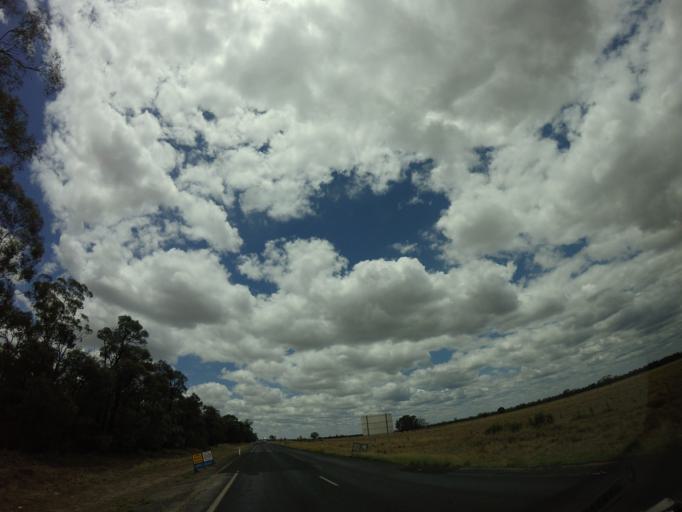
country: AU
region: Queensland
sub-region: Goondiwindi
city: Goondiwindi
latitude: -28.1568
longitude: 150.6663
